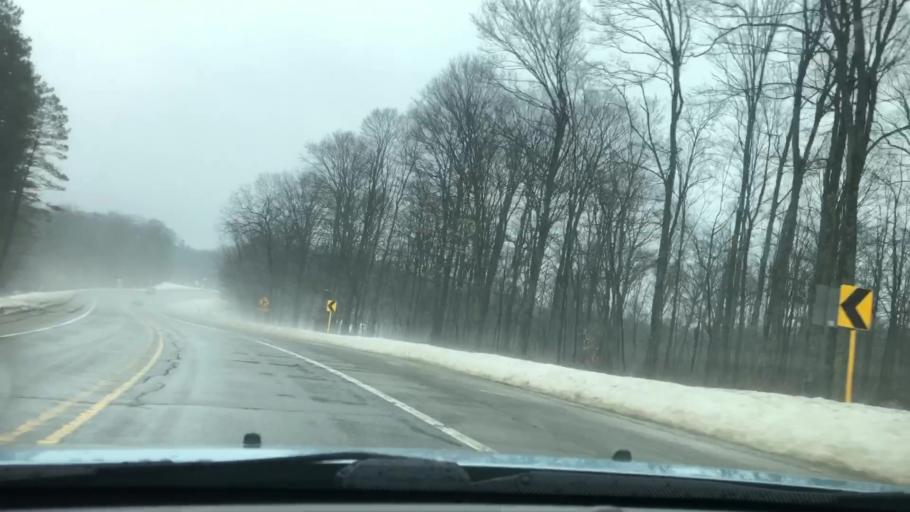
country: US
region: Michigan
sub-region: Otsego County
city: Gaylord
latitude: 45.0600
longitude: -84.7928
